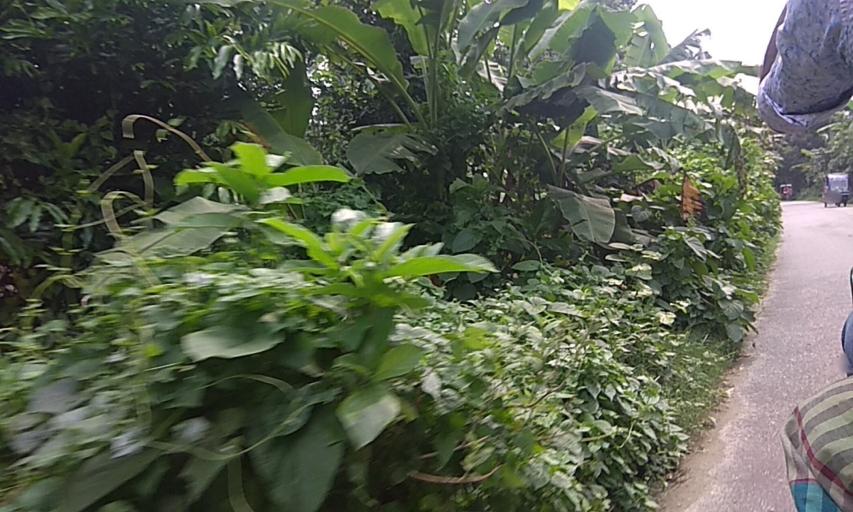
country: BD
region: Dhaka
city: Dohar
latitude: 23.4743
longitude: 90.0430
